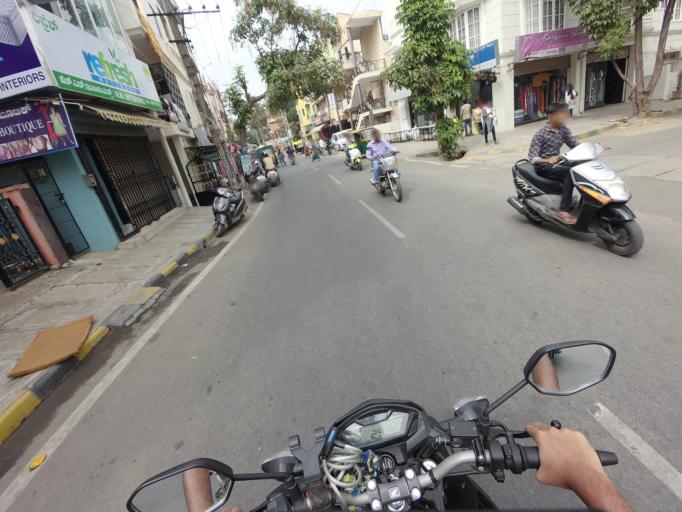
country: IN
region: Karnataka
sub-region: Bangalore Urban
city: Bangalore
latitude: 12.9741
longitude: 77.5353
